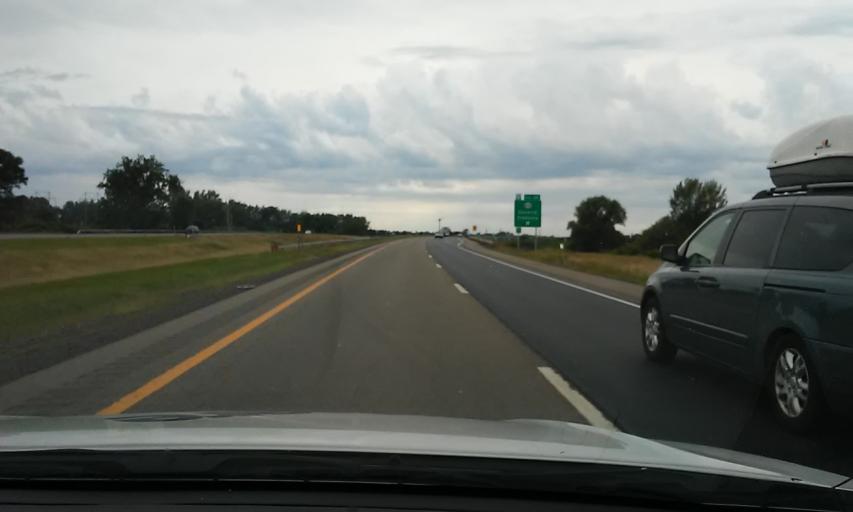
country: US
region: New York
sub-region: Chautauqua County
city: Dunkirk
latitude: 42.4645
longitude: -79.2962
